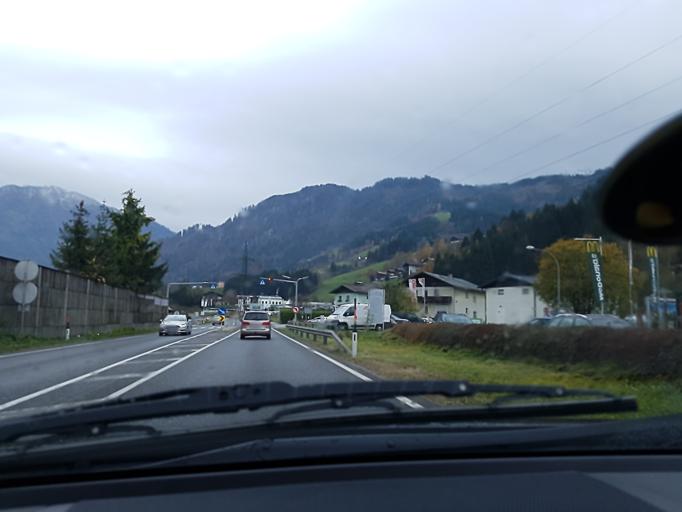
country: AT
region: Salzburg
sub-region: Politischer Bezirk Sankt Johann im Pongau
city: Sankt Johann im Pongau
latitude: 47.3541
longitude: 13.1957
